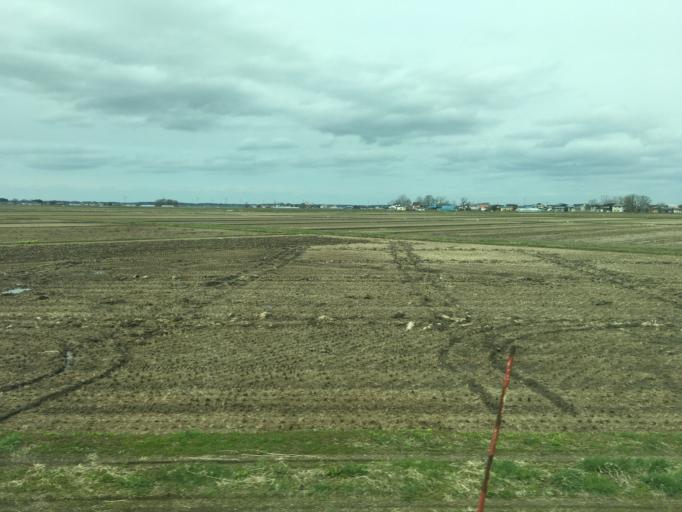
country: JP
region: Aomori
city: Shimokizukuri
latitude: 40.7837
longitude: 140.3583
